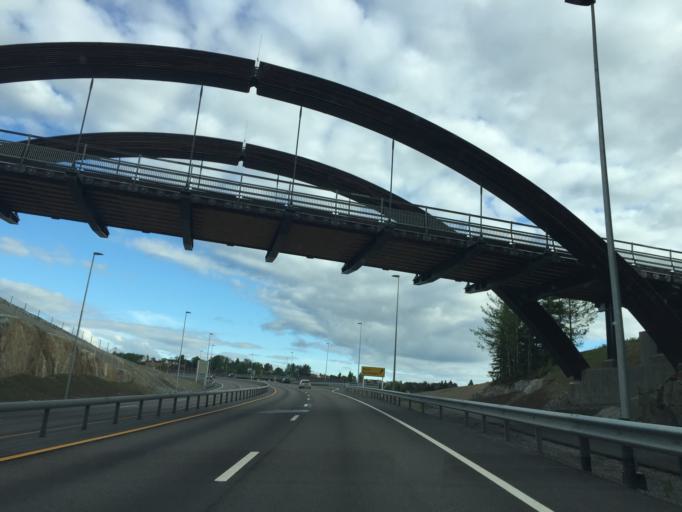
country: NO
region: Akershus
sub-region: Fet
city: Fetsund
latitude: 59.9361
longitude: 11.1346
